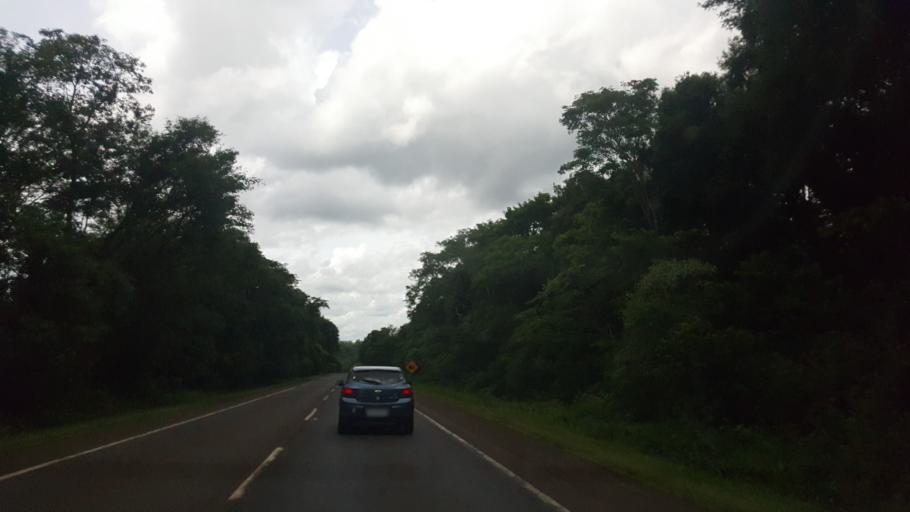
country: AR
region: Misiones
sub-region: Departamento de Iguazu
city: Puerto Iguazu
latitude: -25.6869
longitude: -54.5123
